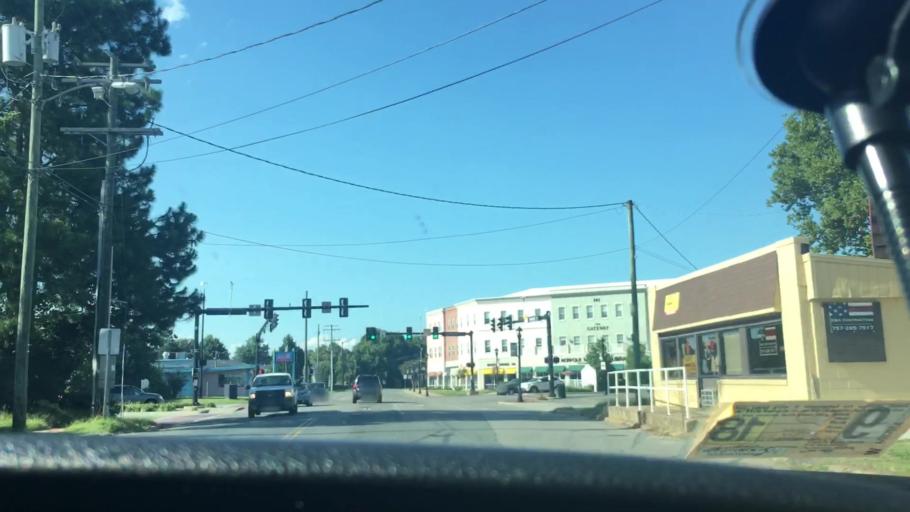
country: US
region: Virginia
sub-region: City of Chesapeake
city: Chesapeake
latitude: 36.8151
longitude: -76.2786
